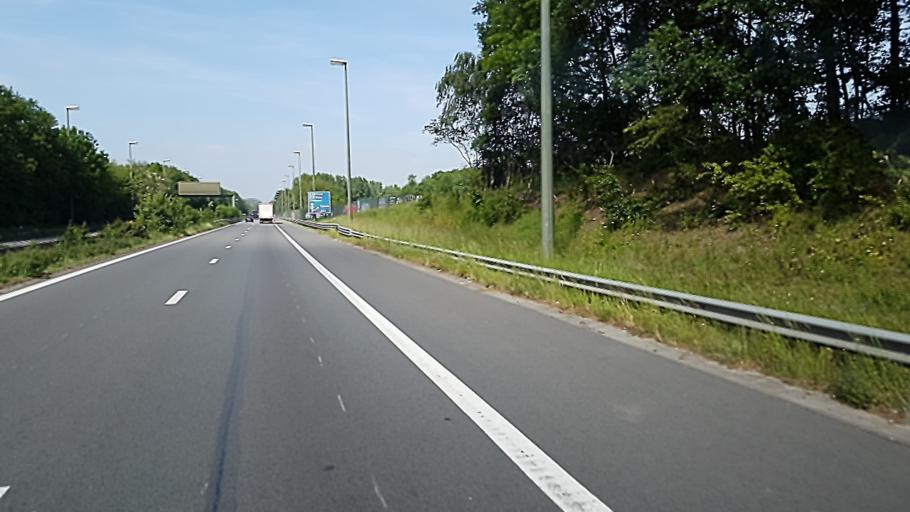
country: BE
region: Wallonia
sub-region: Province du Brabant Wallon
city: Braine-l'Alleud
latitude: 50.6596
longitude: 4.3625
